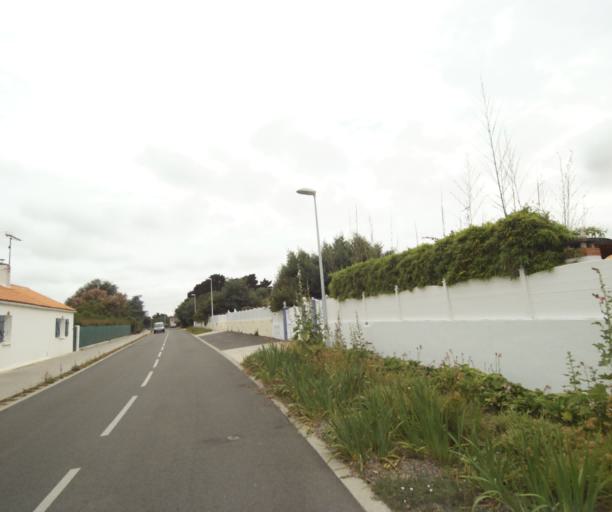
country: FR
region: Pays de la Loire
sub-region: Departement de la Vendee
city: Chateau-d'Olonne
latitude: 46.4721
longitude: -1.7148
